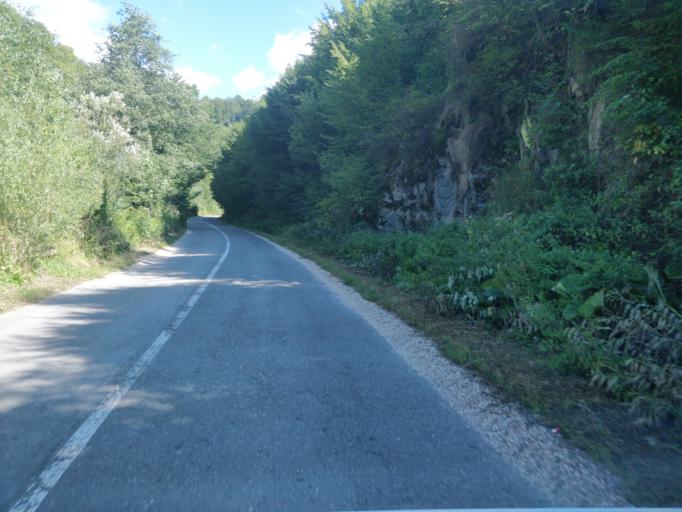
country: RO
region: Cluj
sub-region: Comuna Sacueu
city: Sacuieu
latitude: 46.8376
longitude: 22.8616
